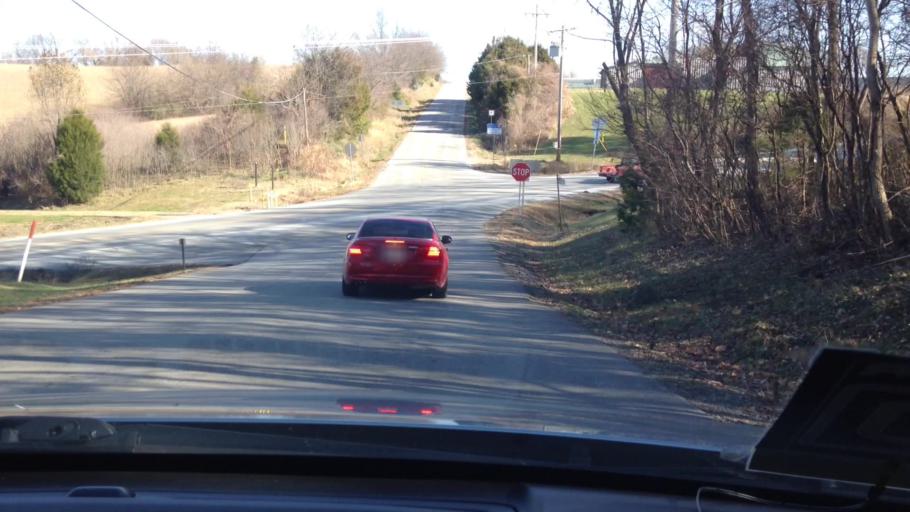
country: US
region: Missouri
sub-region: Platte County
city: Weston
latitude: 39.4177
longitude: -94.8920
